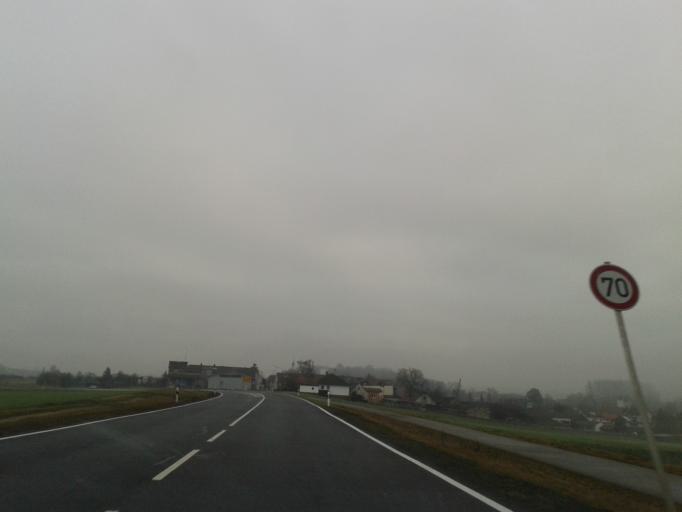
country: DE
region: Bavaria
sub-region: Regierungsbezirk Unterfranken
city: Pfarrweisach
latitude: 50.1925
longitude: 10.7540
